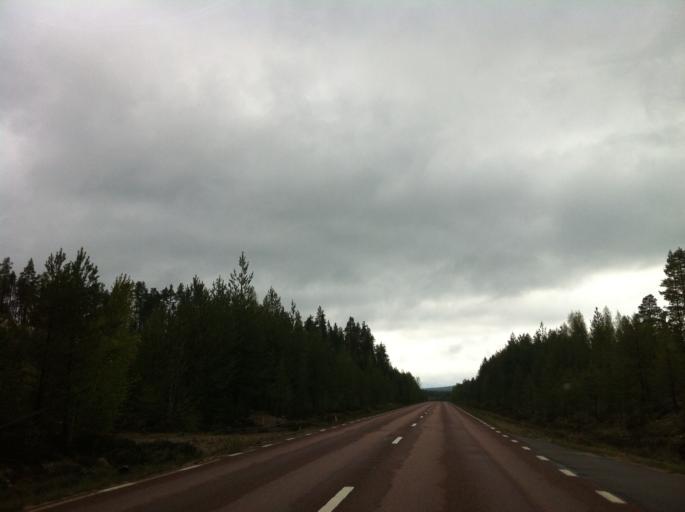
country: SE
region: Jaemtland
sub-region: Harjedalens Kommun
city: Sveg
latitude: 61.9721
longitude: 14.5765
